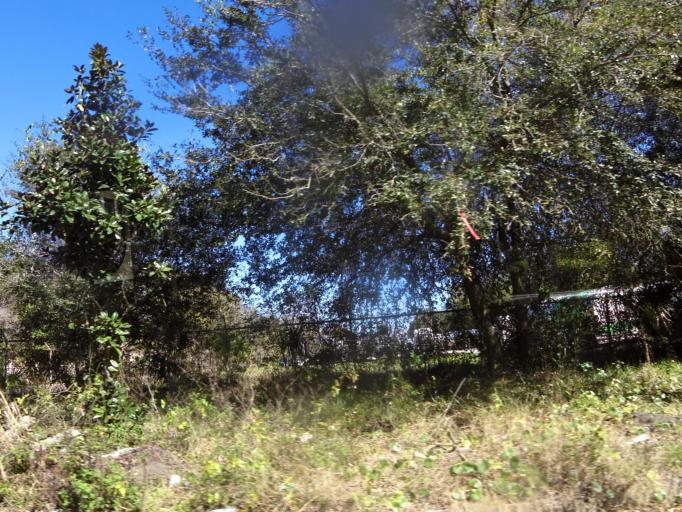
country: US
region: Florida
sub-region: Duval County
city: Jacksonville
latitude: 30.3617
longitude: -81.6307
